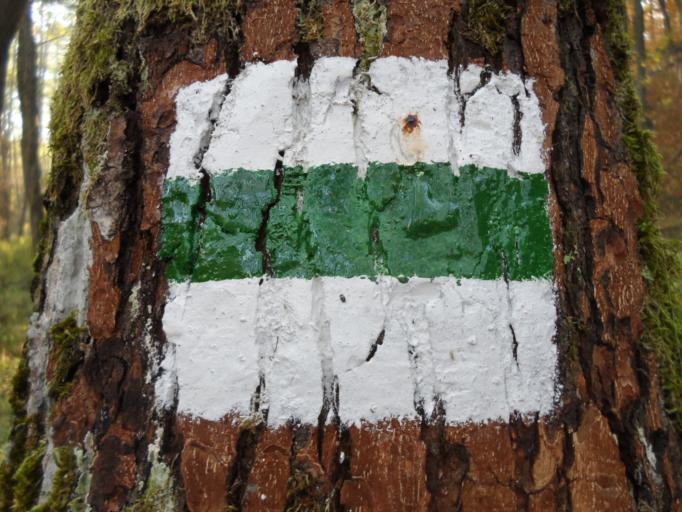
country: HU
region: Veszprem
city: Ajka
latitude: 47.1900
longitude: 17.5895
